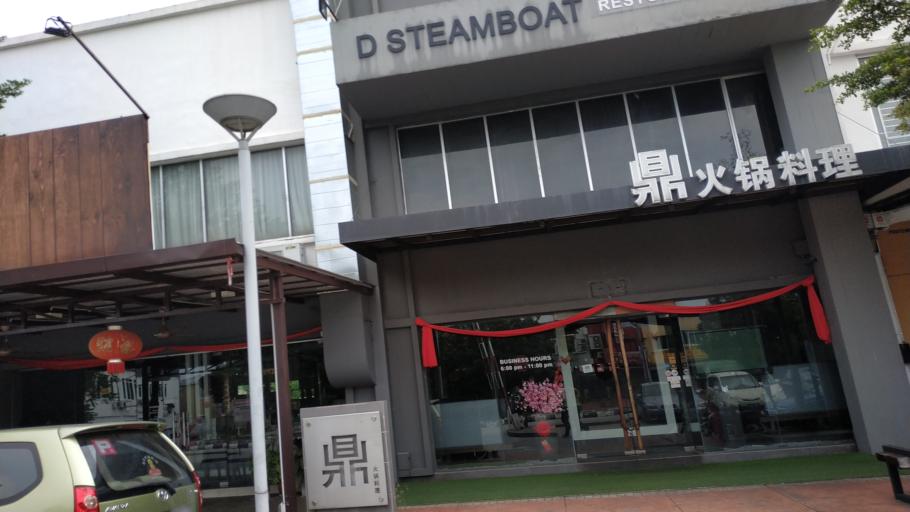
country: MY
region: Perak
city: Ipoh
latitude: 4.6192
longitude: 101.1187
